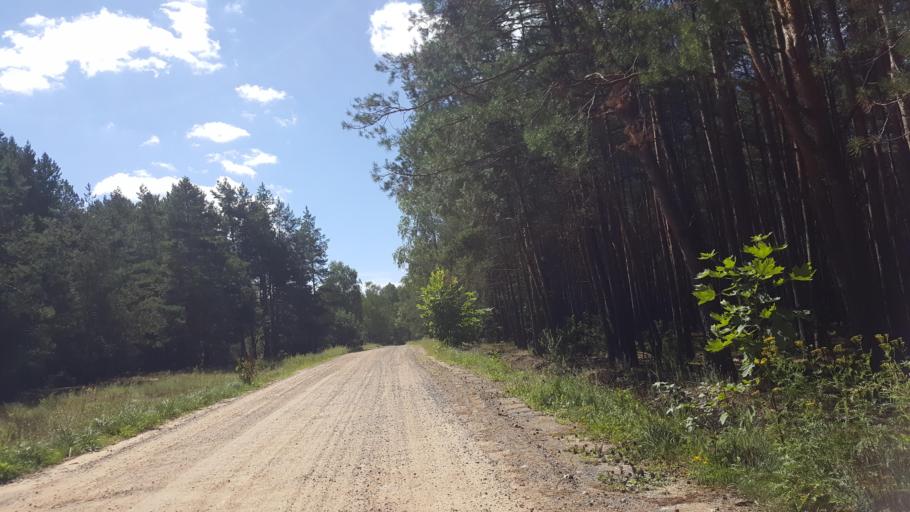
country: BY
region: Brest
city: Zhabinka
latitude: 52.3994
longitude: 24.0894
